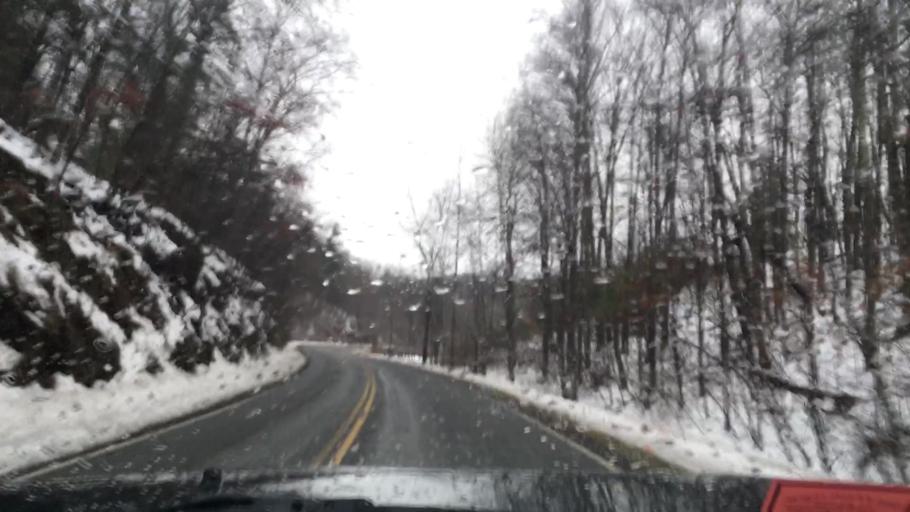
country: US
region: Virginia
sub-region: Pulaski County
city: Pulaski
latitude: 37.0180
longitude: -80.7070
